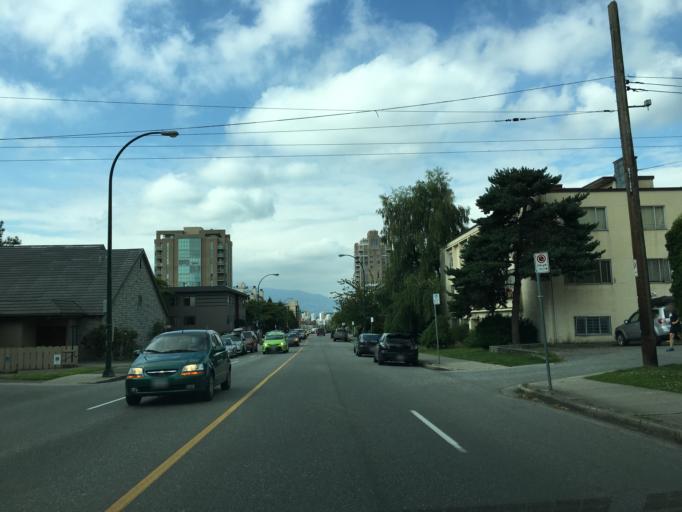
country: CA
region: British Columbia
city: West End
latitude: 49.2611
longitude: -123.1411
